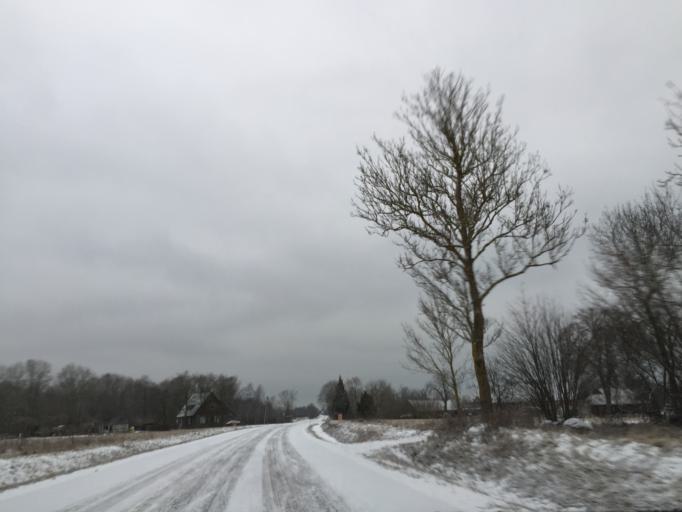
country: EE
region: Saare
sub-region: Orissaare vald
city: Orissaare
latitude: 58.6479
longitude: 23.2934
